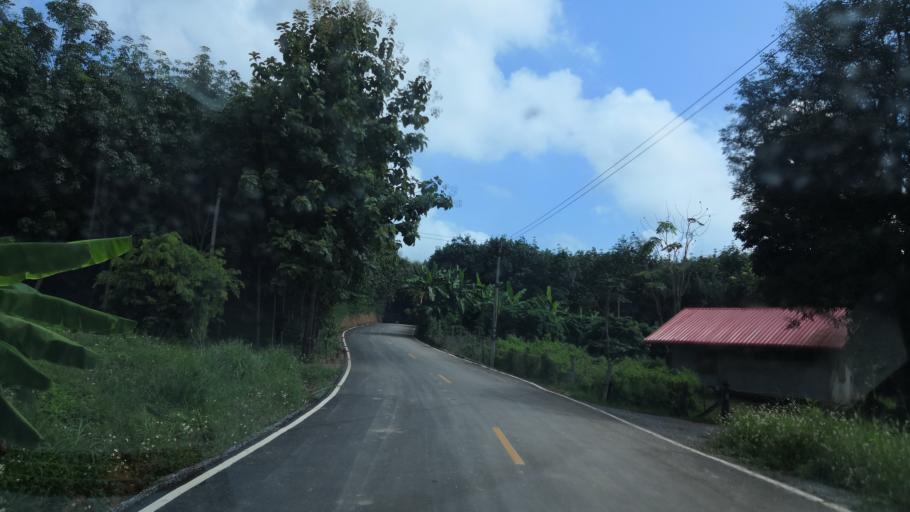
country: TH
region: Chiang Rai
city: Wiang Chiang Rung
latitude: 20.0250
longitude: 100.0496
